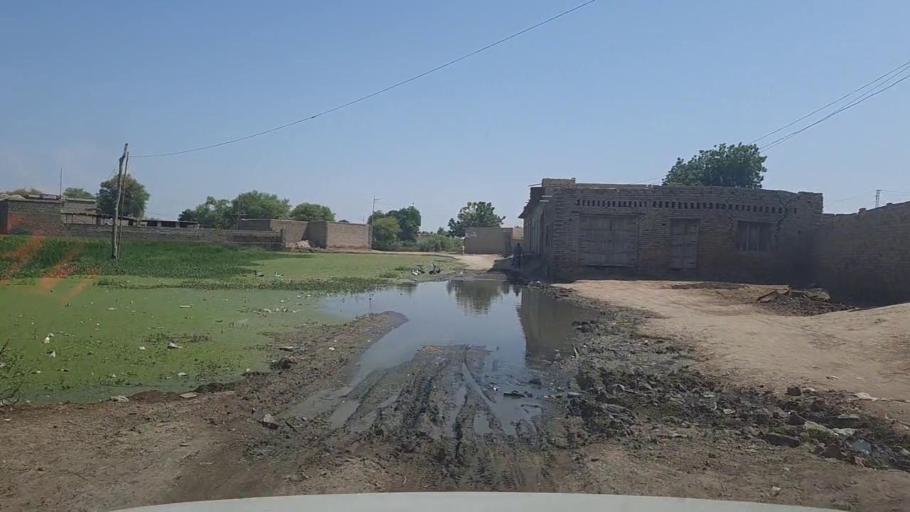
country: PK
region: Sindh
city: Kashmor
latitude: 28.2997
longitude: 69.4250
